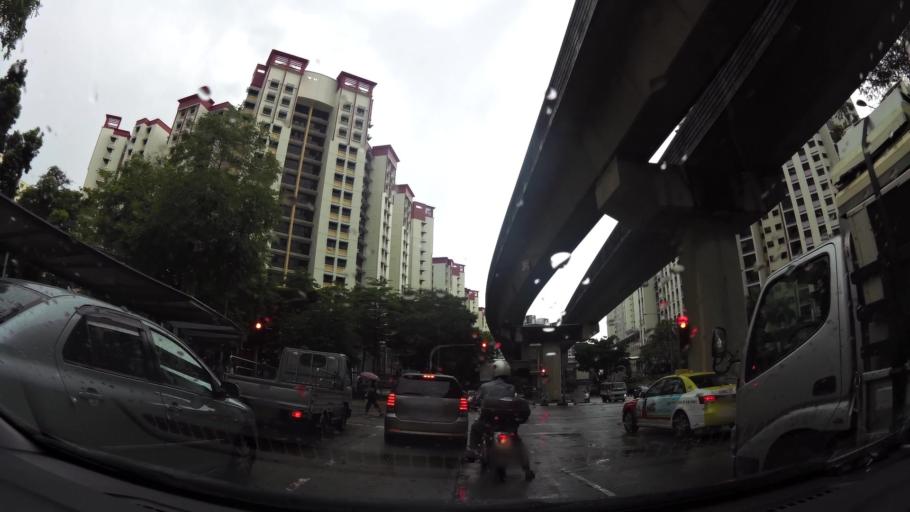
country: MY
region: Johor
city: Kampung Pasir Gudang Baru
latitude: 1.3925
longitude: 103.9053
